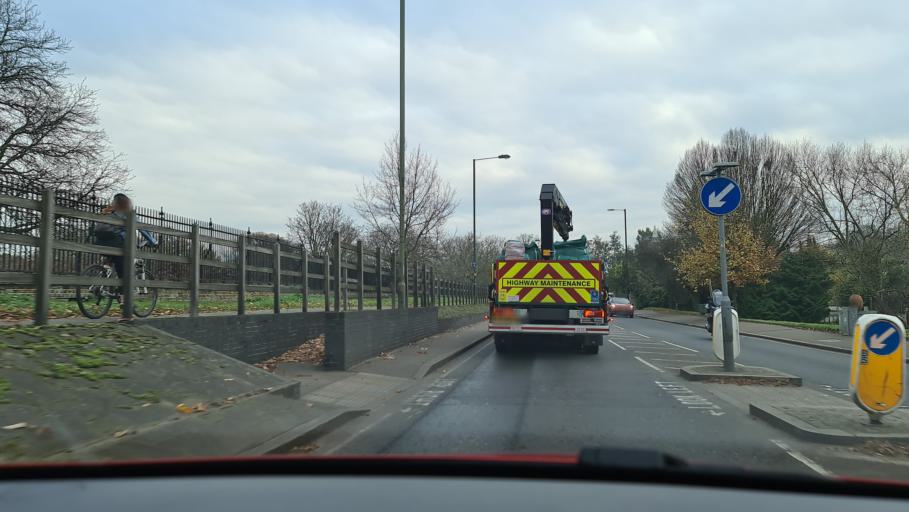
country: GB
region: England
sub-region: Surrey
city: East Molesey
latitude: 51.4098
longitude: -0.3509
